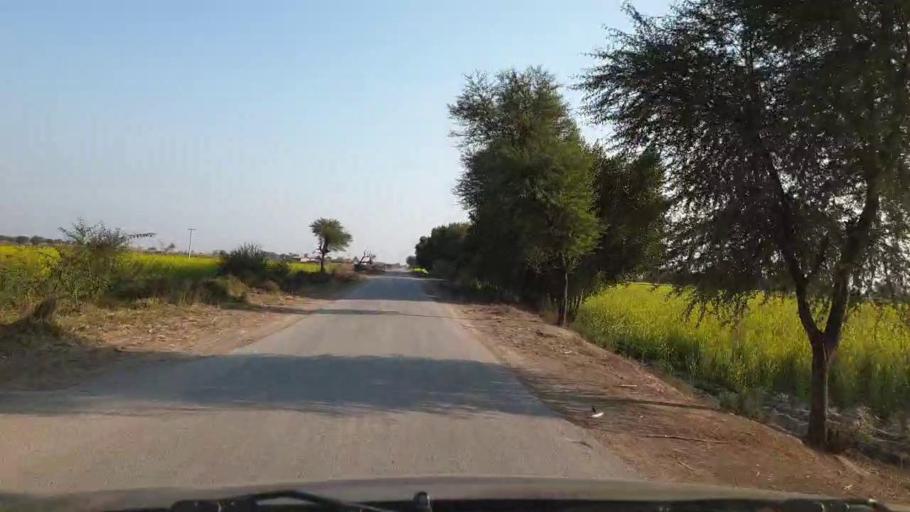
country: PK
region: Sindh
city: Jhol
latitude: 25.9491
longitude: 68.9033
